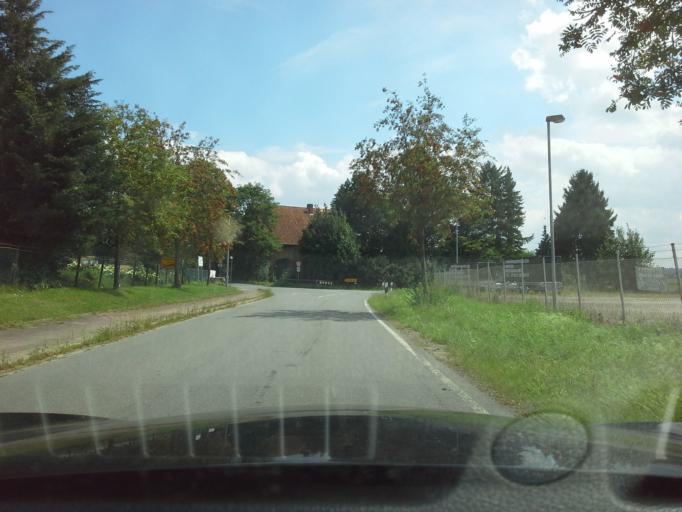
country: DE
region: Lower Saxony
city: Messenkamp
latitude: 52.2589
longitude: 9.3840
